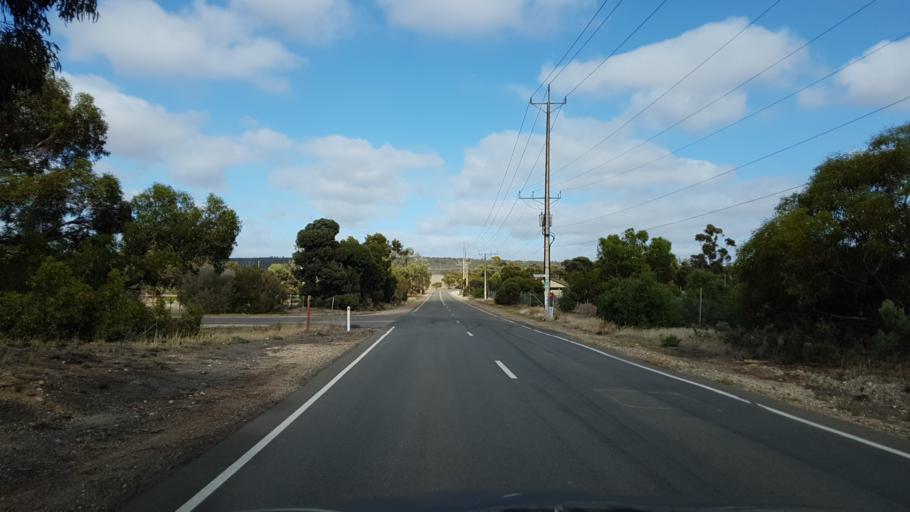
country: AU
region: South Australia
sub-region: Murray Bridge
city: Murray Bridge
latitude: -35.1173
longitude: 139.2436
